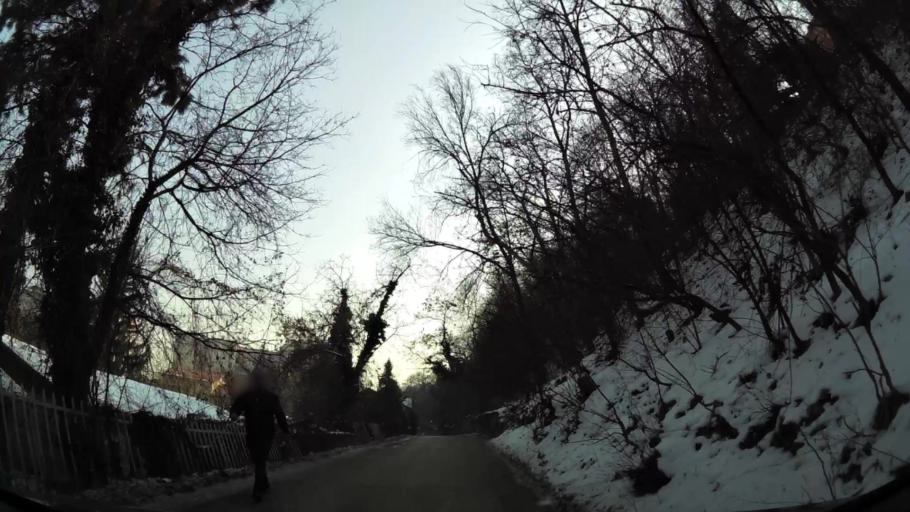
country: MK
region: Karpos
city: Skopje
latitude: 41.9871
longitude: 21.4252
